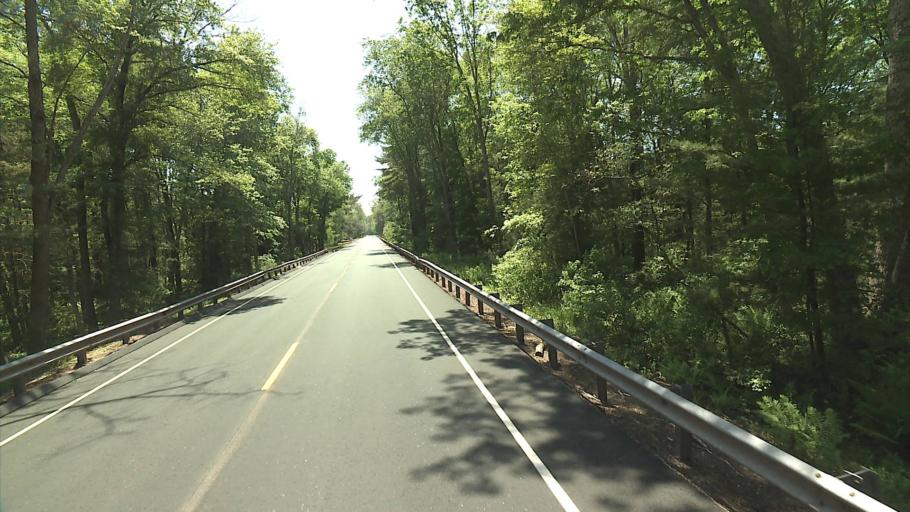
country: US
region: Connecticut
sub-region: Tolland County
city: Crystal Lake
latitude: 41.9569
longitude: -72.3678
